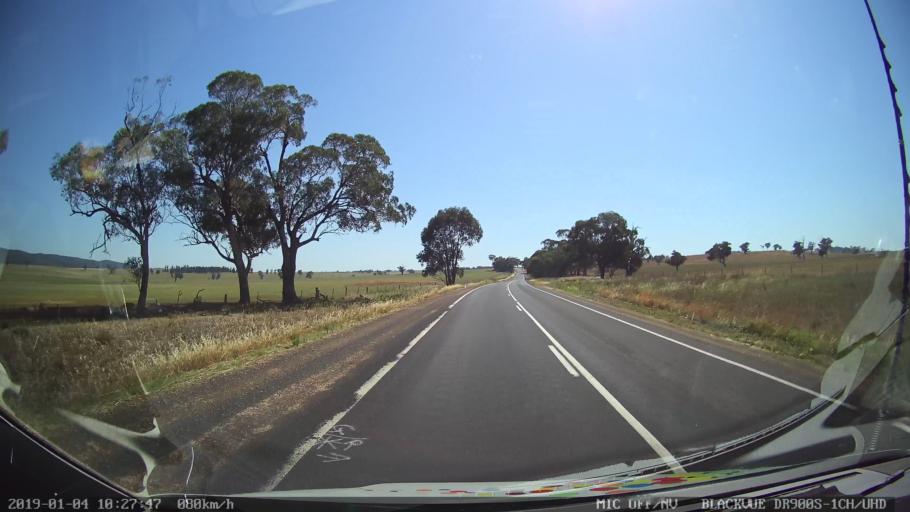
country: AU
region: New South Wales
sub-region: Cabonne
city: Canowindra
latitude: -33.3671
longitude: 148.6019
